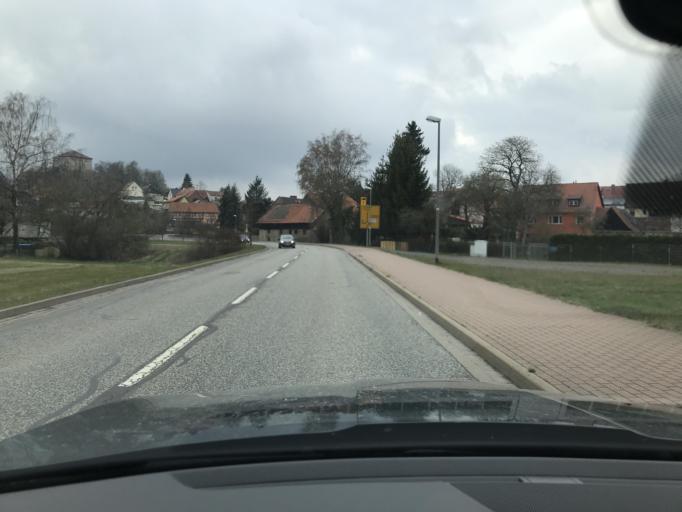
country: DE
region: Saxony-Anhalt
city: Harzgerode
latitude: 51.6399
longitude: 11.1417
